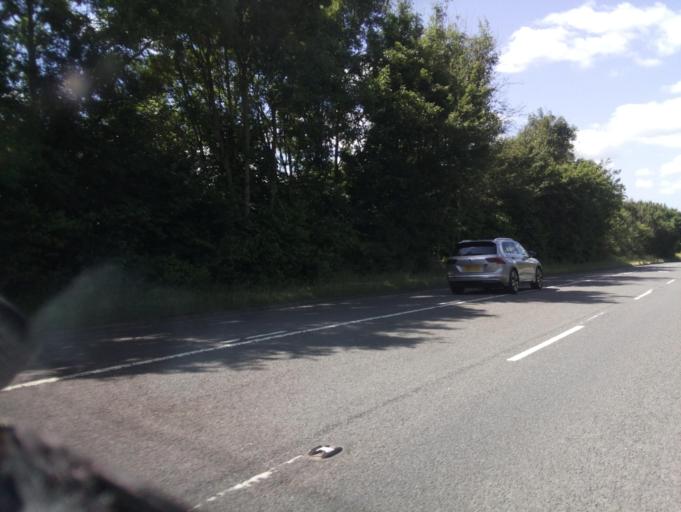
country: GB
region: England
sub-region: Derbyshire
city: Ashbourne
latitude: 53.0054
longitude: -1.7331
